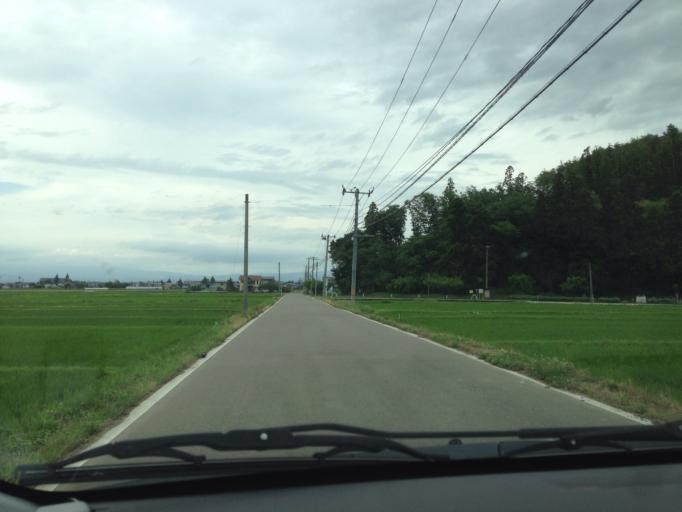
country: JP
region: Fukushima
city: Kitakata
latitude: 37.4410
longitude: 139.8900
